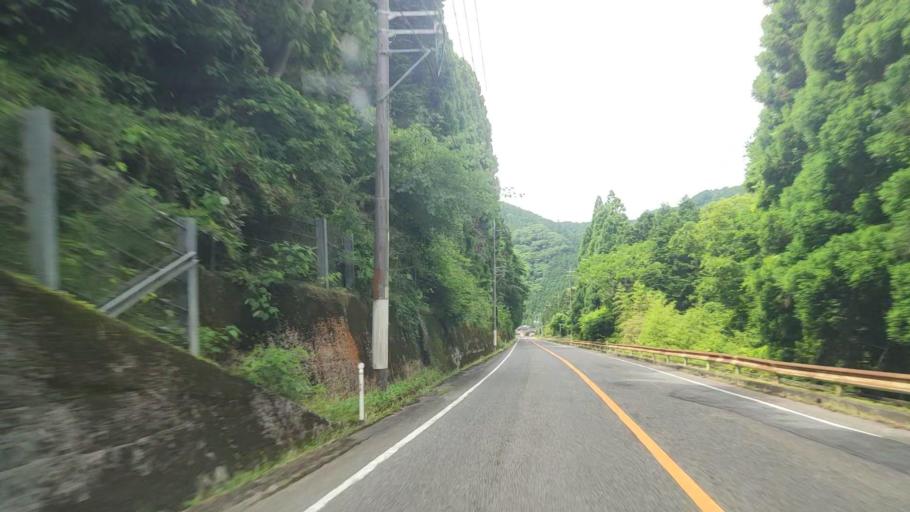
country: JP
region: Okayama
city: Niimi
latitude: 35.0881
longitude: 133.6484
